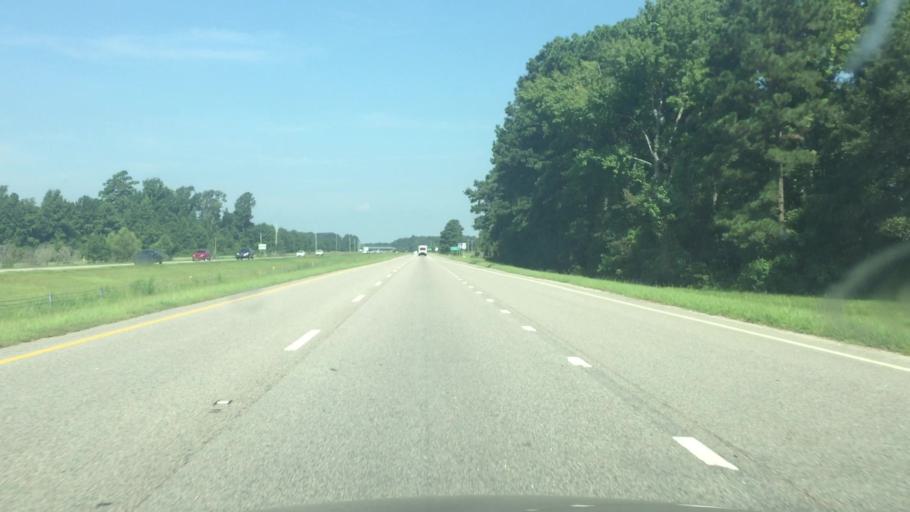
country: US
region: North Carolina
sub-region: Robeson County
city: Lumberton
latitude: 34.5826
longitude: -79.0531
